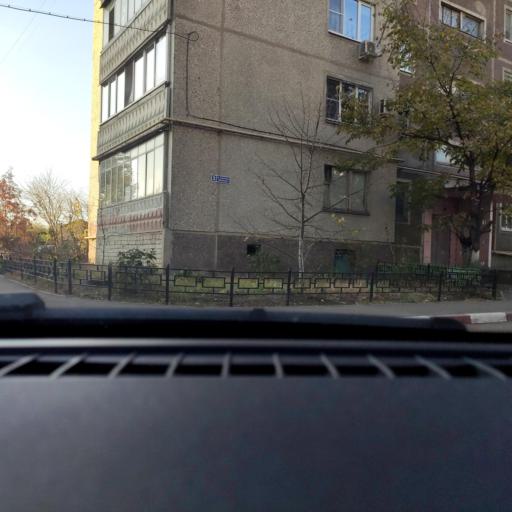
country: RU
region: Voronezj
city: Voronezh
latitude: 51.6732
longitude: 39.2457
